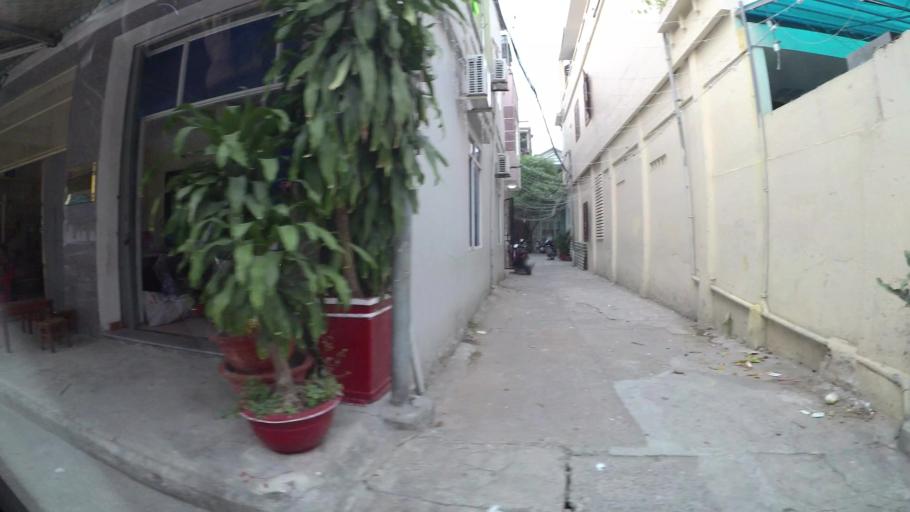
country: VN
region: Da Nang
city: Da Nang
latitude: 16.0739
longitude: 108.2215
